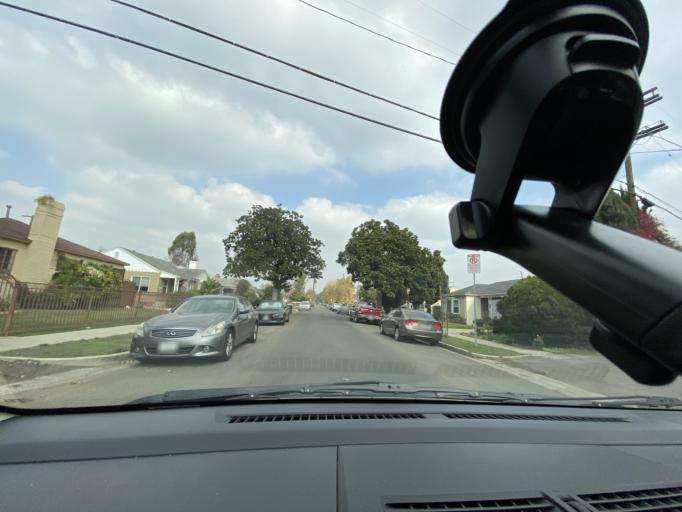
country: US
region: California
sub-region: Los Angeles County
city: Culver City
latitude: 34.0317
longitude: -118.3977
